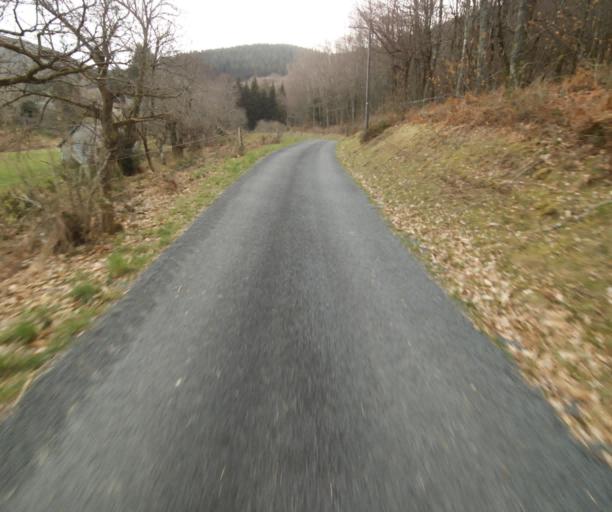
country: FR
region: Limousin
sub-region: Departement de la Correze
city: Treignac
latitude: 45.4710
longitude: 1.8288
